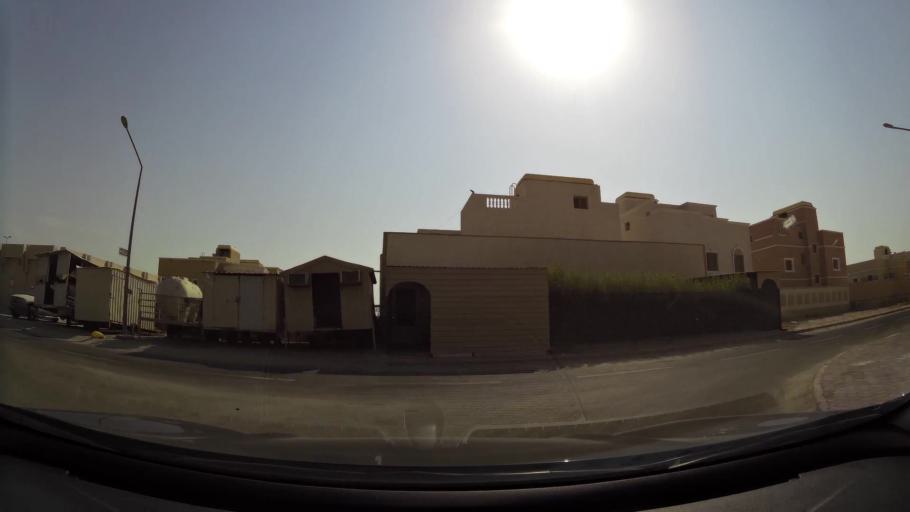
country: KW
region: Al Ahmadi
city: Al Wafrah
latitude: 28.7926
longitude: 48.0735
